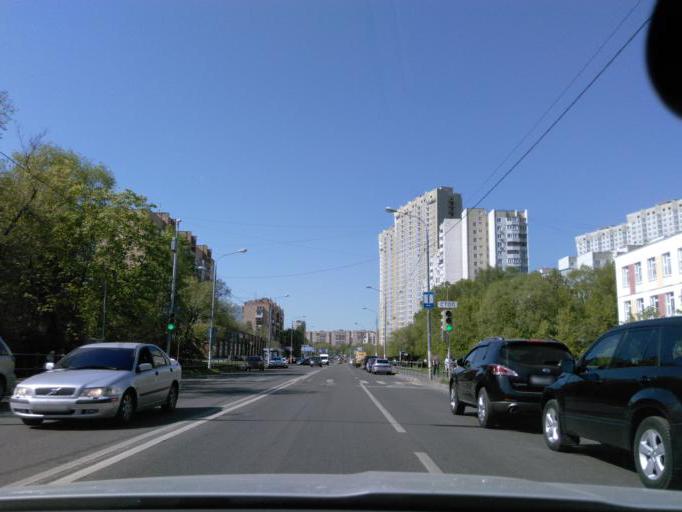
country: RU
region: Moscow
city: Golovinskiy
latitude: 55.8550
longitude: 37.5035
